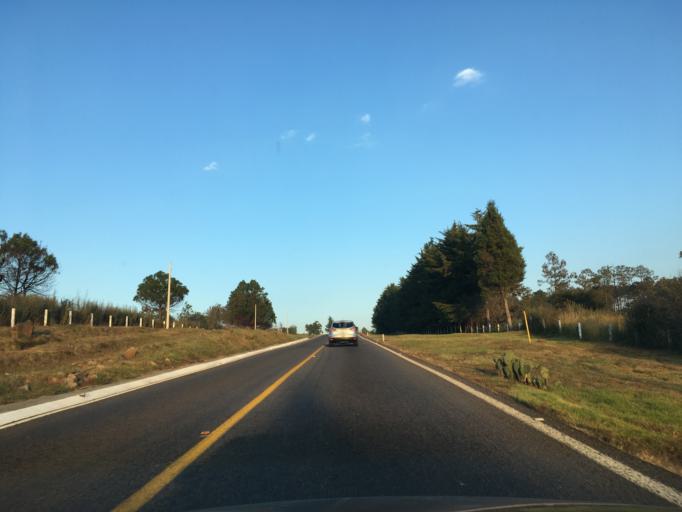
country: MX
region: Michoacan
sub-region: Patzcuaro
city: Santa Ana Chapitiro
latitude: 19.5109
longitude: -101.6771
